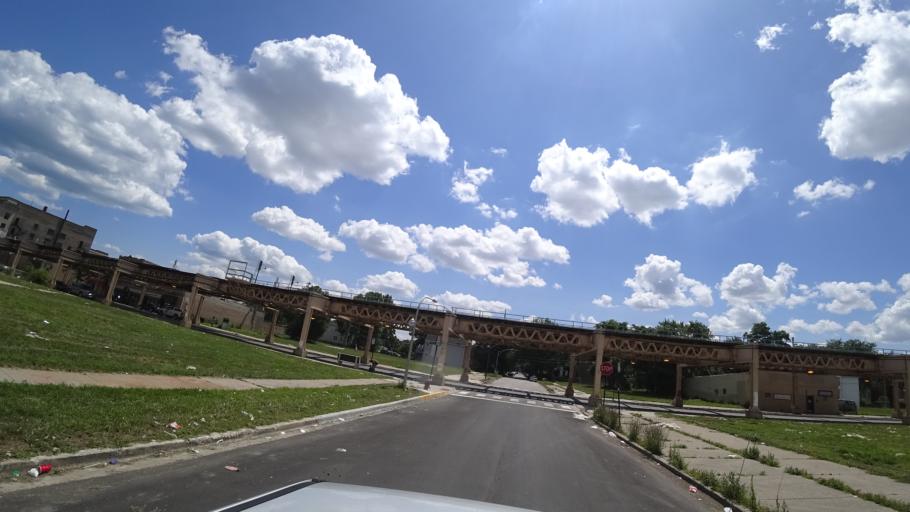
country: US
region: Illinois
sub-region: Cook County
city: Chicago
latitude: 41.7807
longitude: -87.6084
